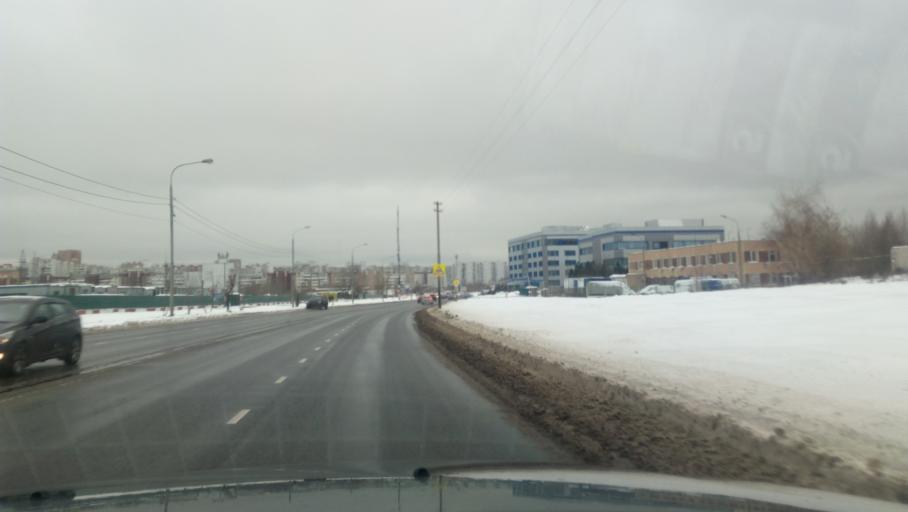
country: RU
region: Moscow
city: Zhulebino
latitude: 55.7254
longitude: 37.8588
